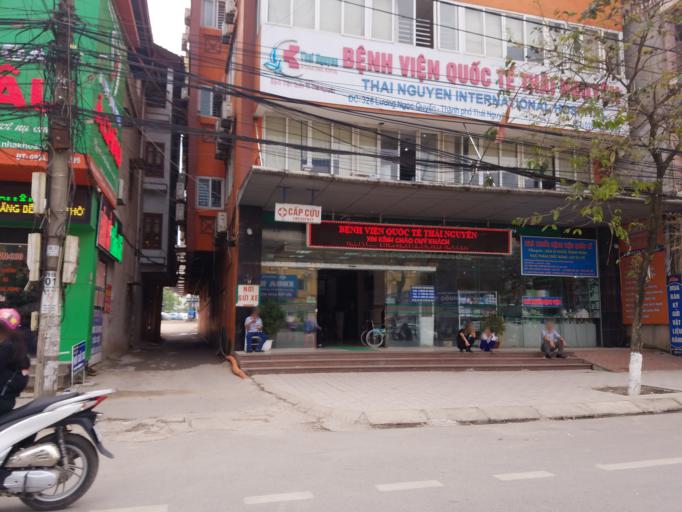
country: VN
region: Thai Nguyen
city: Thanh Pho Thai Nguyen
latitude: 21.5875
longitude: 105.8298
